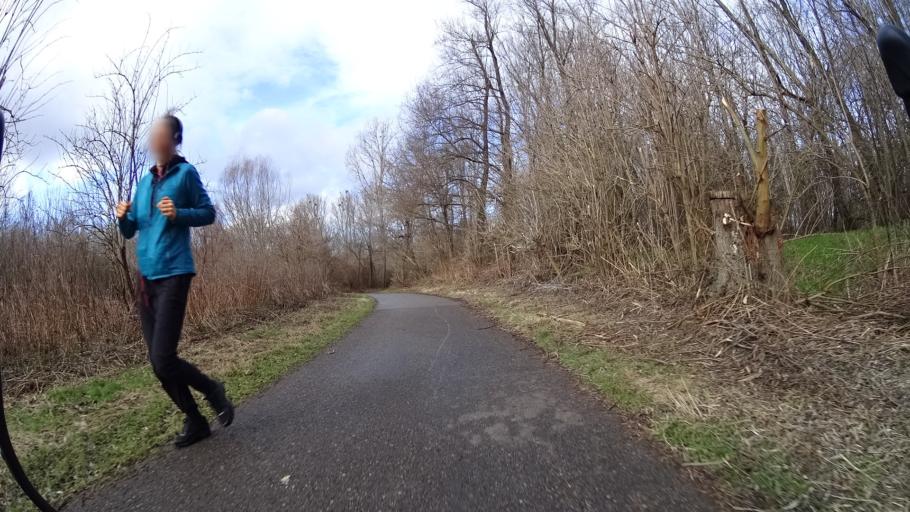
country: AT
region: Lower Austria
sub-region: Politischer Bezirk Tulln
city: Atzenbrugg
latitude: 48.3585
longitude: 15.8804
